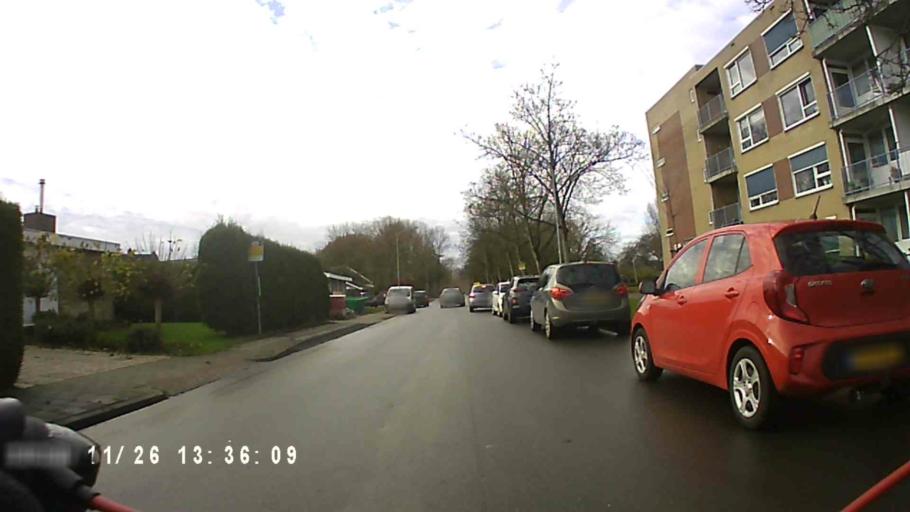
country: NL
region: Groningen
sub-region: Gemeente Delfzijl
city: Delfzijl
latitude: 53.3349
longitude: 6.9210
